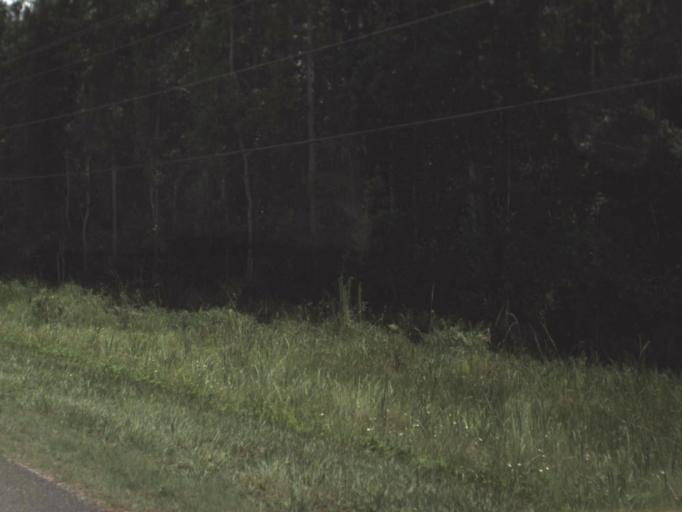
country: US
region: Florida
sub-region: Clay County
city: Keystone Heights
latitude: 29.7384
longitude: -82.0503
